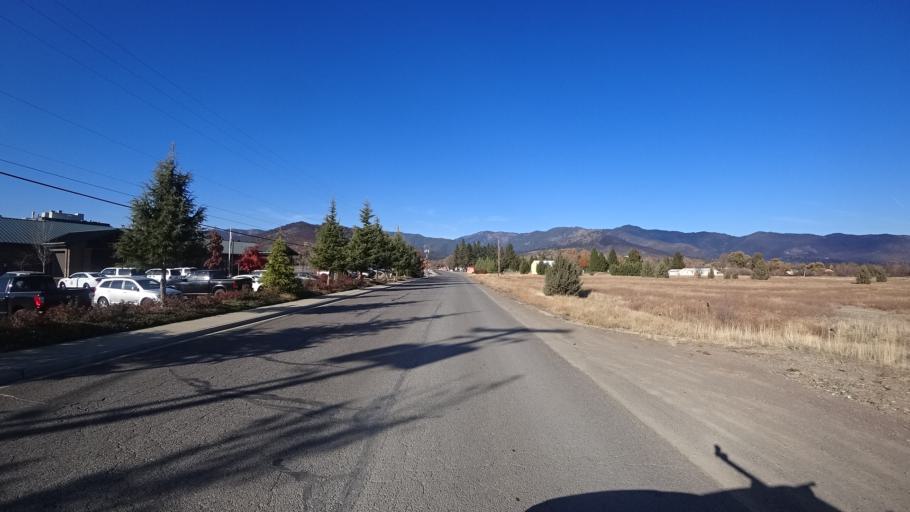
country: US
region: California
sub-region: Siskiyou County
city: Yreka
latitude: 41.7087
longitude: -122.6345
